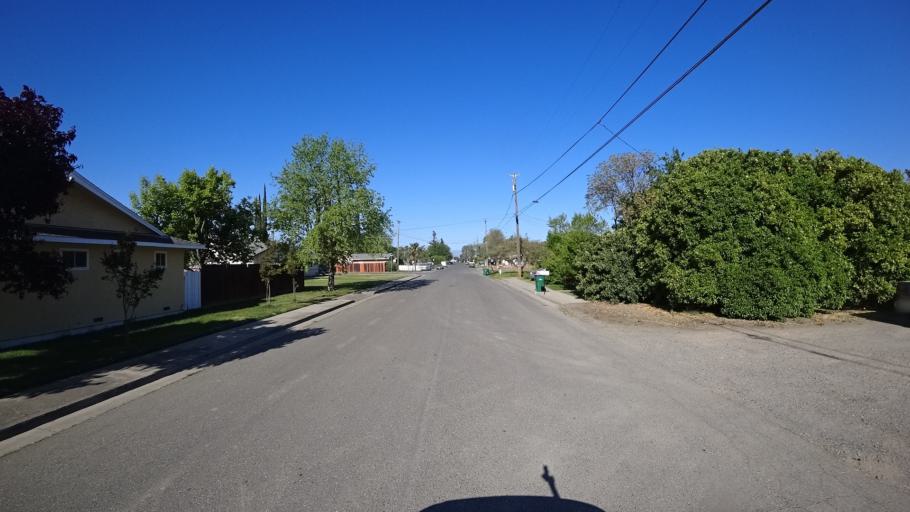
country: US
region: California
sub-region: Glenn County
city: Orland
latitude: 39.7416
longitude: -122.1891
